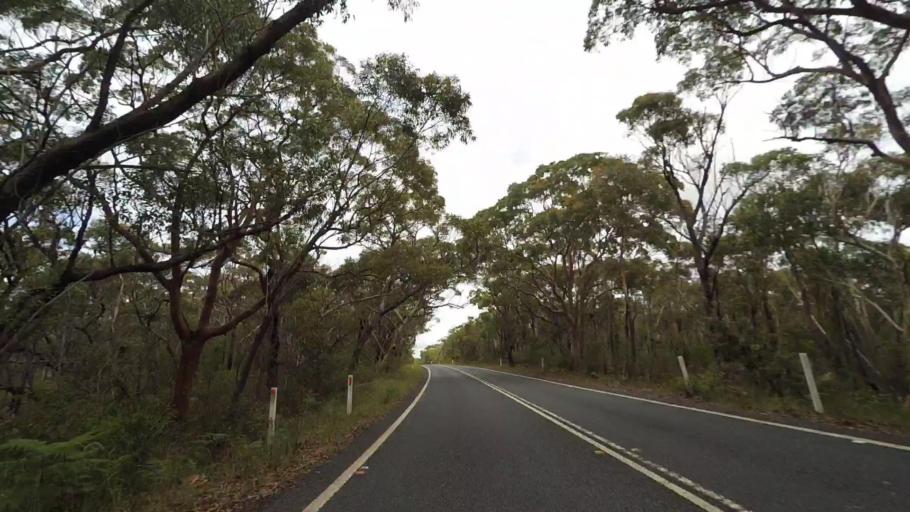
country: AU
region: New South Wales
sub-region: Sutherland Shire
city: Grays Point
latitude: -34.0970
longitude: 151.0601
